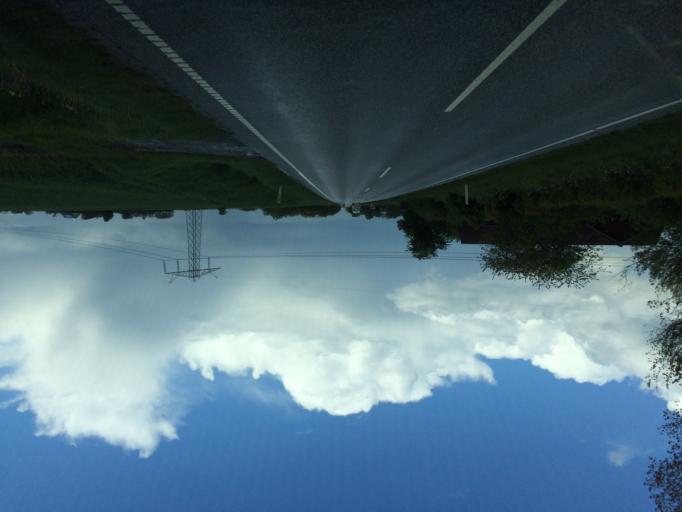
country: DK
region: Central Jutland
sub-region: Holstebro Kommune
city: Holstebro
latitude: 56.3971
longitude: 8.6696
